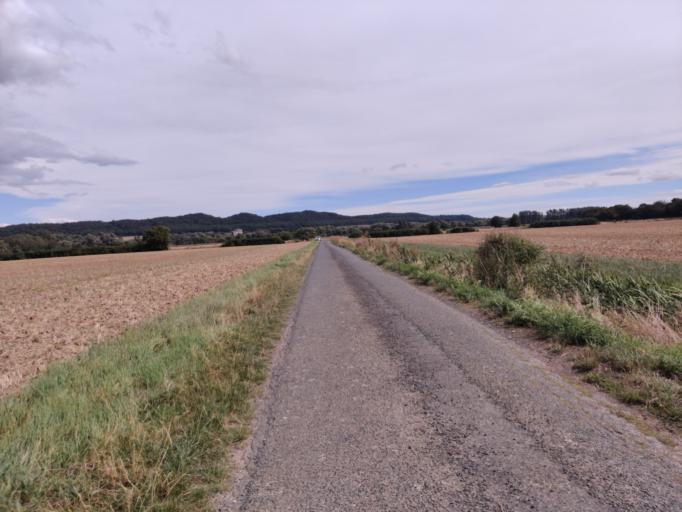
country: DE
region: Lower Saxony
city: Alt Wallmoden
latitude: 52.0101
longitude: 10.3574
